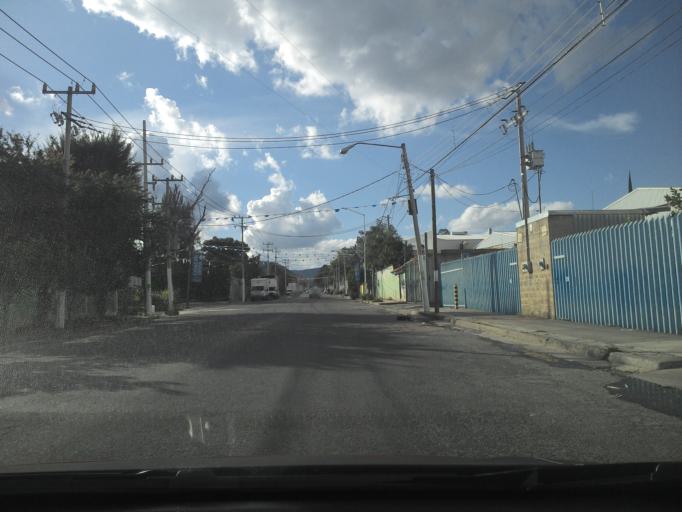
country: MX
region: Jalisco
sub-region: Tlajomulco de Zuniga
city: Palomar
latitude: 20.6156
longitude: -103.4420
